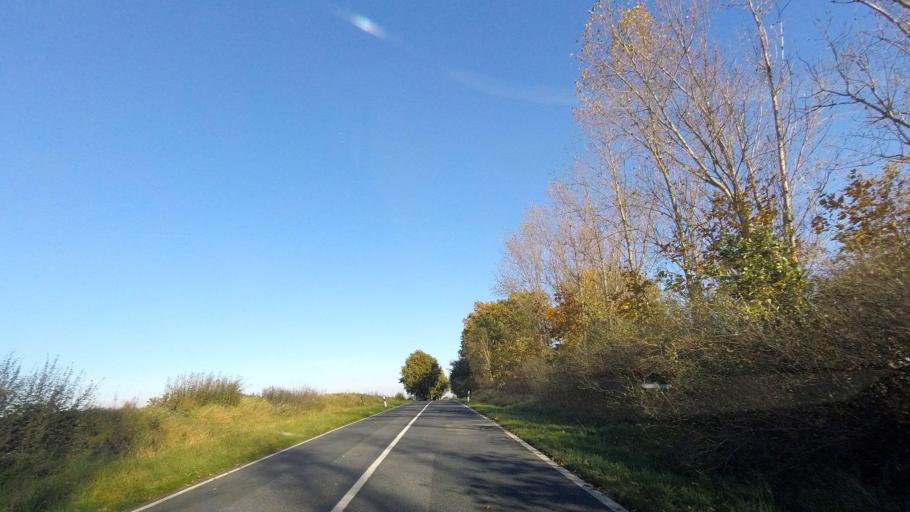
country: DE
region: Brandenburg
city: Treuenbrietzen
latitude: 51.9924
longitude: 12.8796
